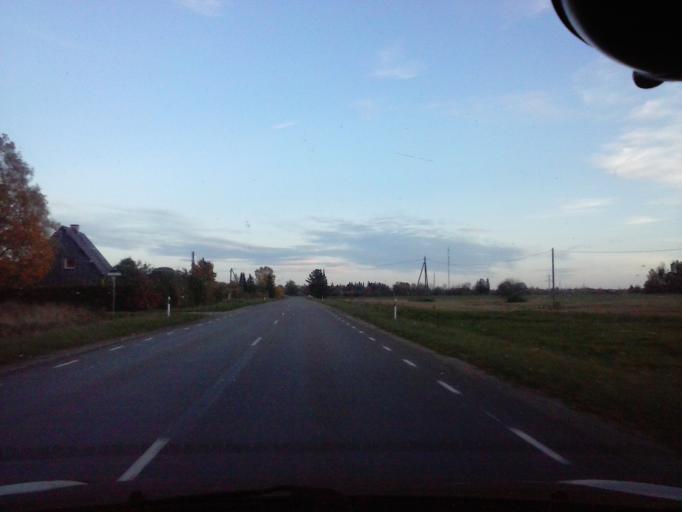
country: EE
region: Raplamaa
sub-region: Maerjamaa vald
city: Marjamaa
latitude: 58.9188
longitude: 24.4154
